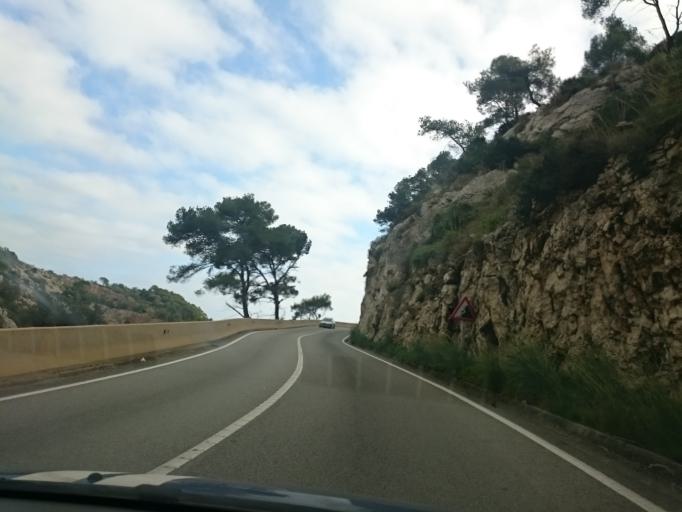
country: ES
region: Catalonia
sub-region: Provincia de Barcelona
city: Sitges
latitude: 41.2516
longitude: 1.8885
